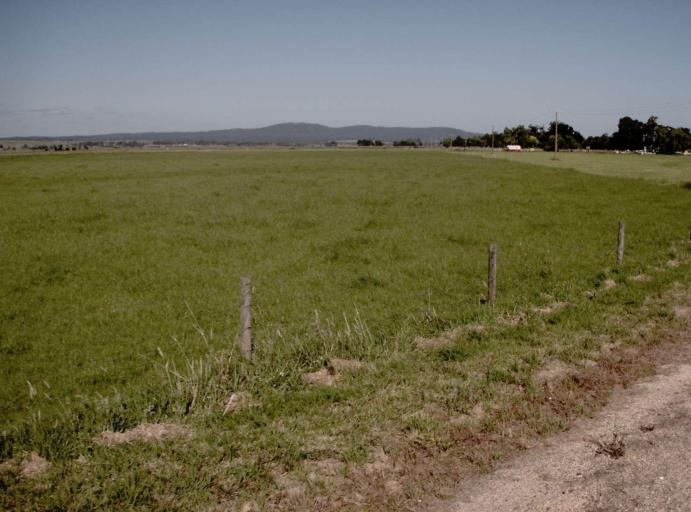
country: AU
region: Victoria
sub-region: East Gippsland
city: Lakes Entrance
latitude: -37.7194
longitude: 148.4733
